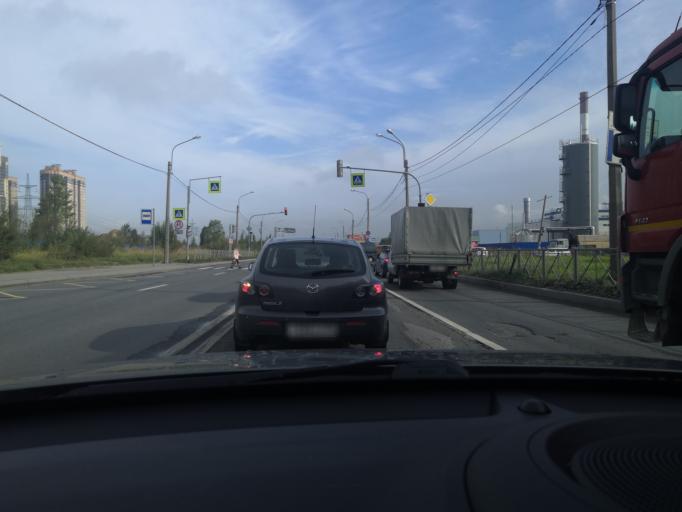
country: RU
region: Leningrad
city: Parnas
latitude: 60.0772
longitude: 30.3544
